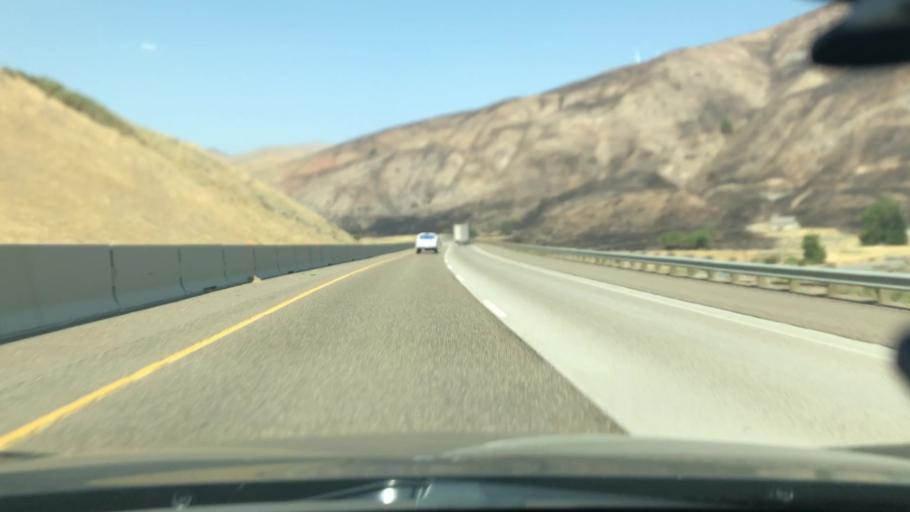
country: US
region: Idaho
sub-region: Washington County
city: Weiser
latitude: 44.4095
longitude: -117.3115
